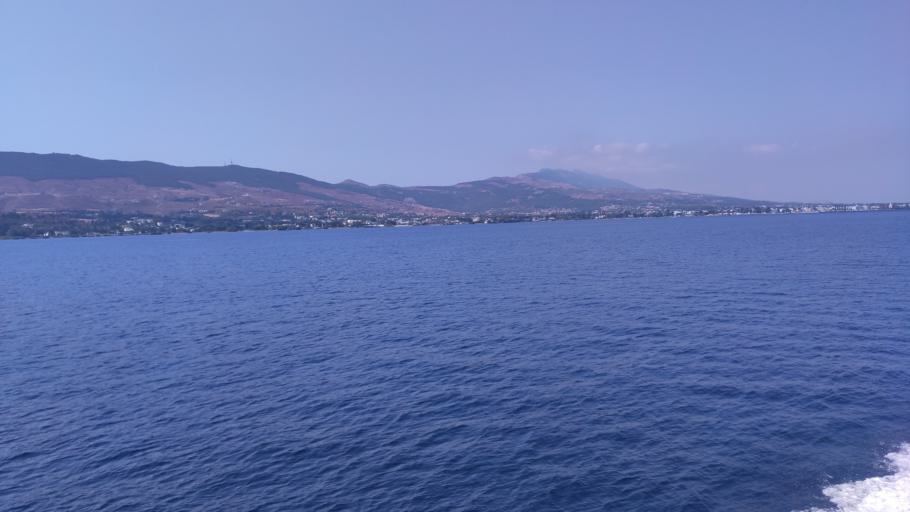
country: GR
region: South Aegean
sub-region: Nomos Dodekanisou
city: Kos
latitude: 36.8972
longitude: 27.3290
